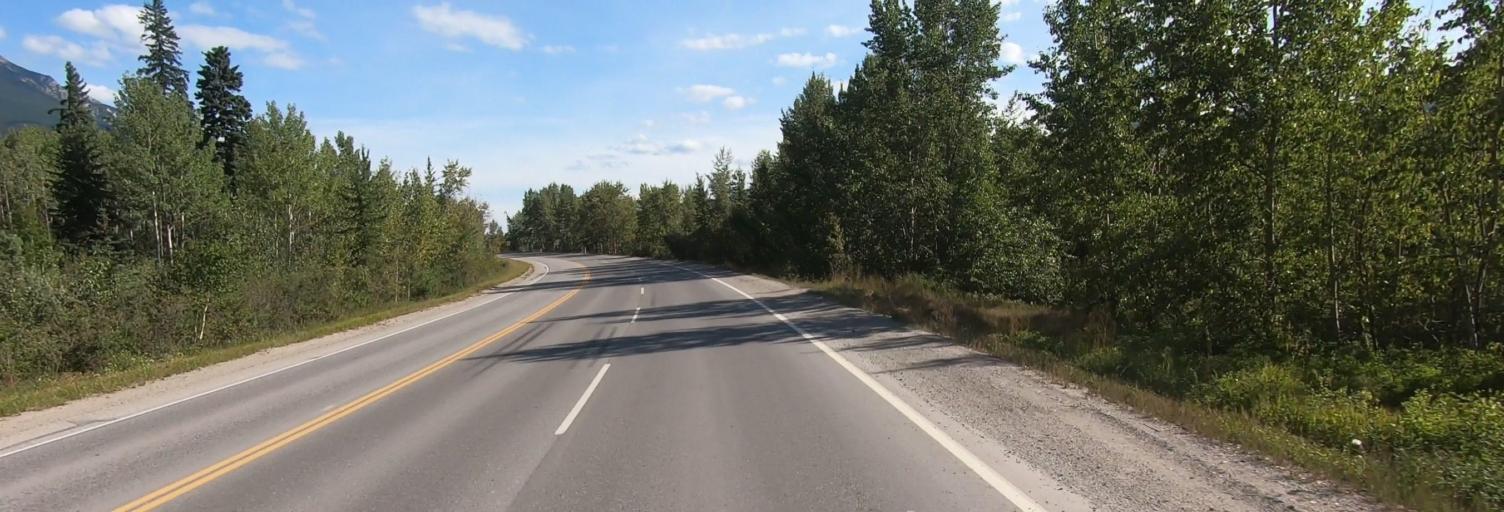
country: CA
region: British Columbia
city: Golden
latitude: 51.2903
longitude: -116.9629
